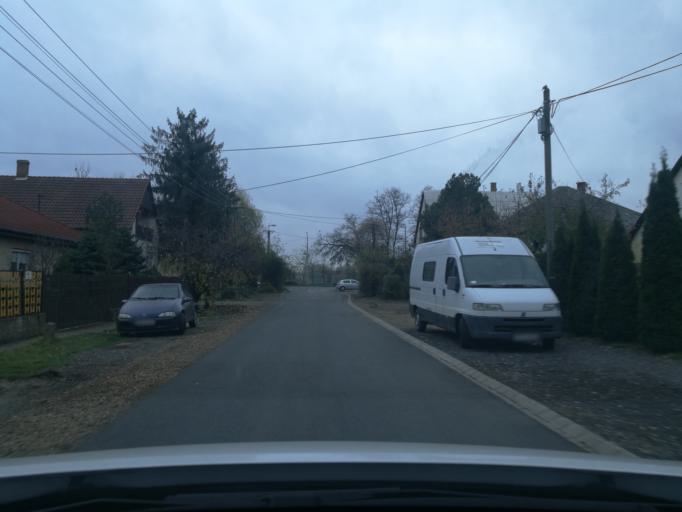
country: HU
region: Szabolcs-Szatmar-Bereg
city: Nyirpazony
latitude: 47.9507
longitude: 21.7822
